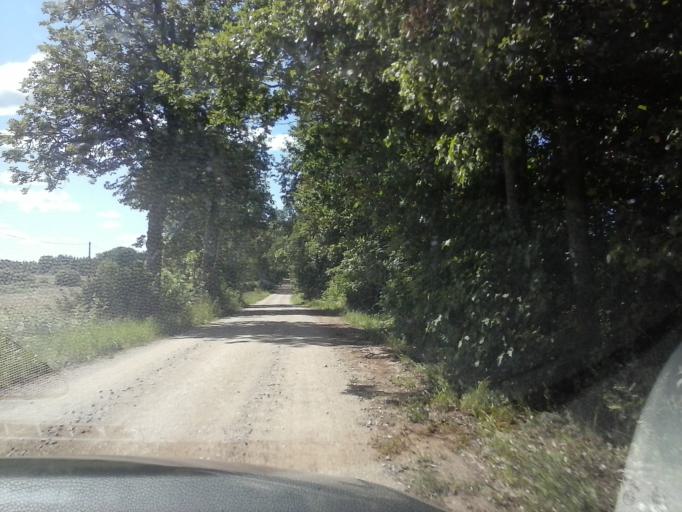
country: LV
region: Apes Novads
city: Ape
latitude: 57.5713
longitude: 26.6765
